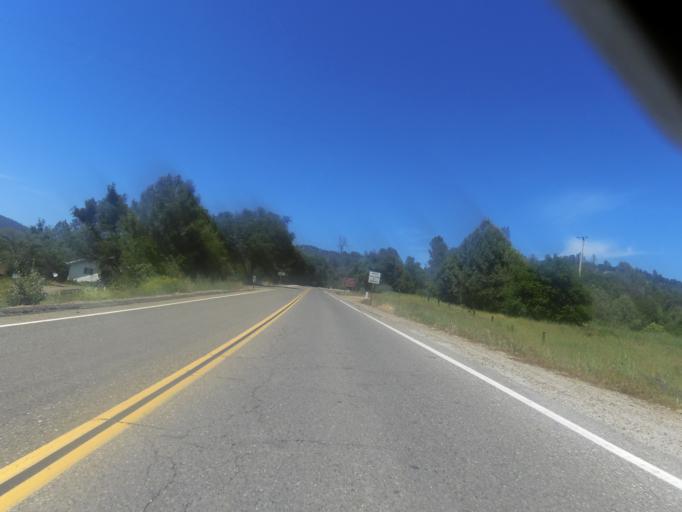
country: US
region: California
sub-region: Mariposa County
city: Mariposa
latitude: 37.4981
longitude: -119.9729
